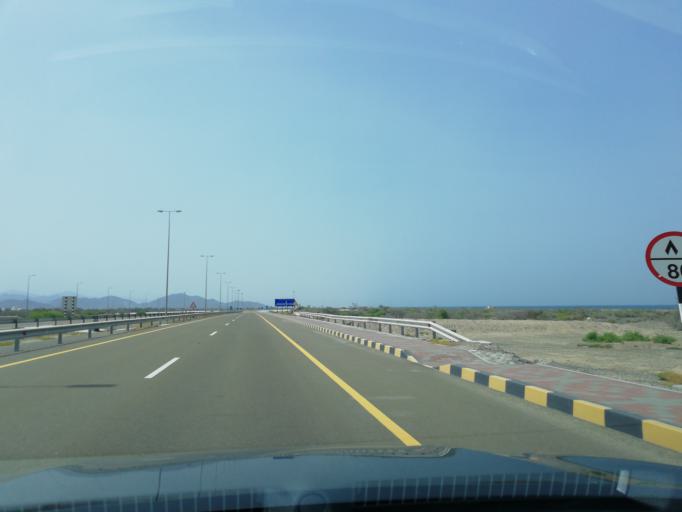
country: OM
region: Al Batinah
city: Shinas
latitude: 24.9128
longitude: 56.3909
